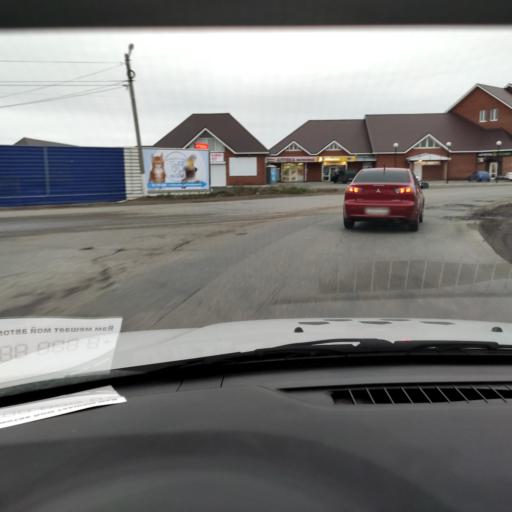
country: RU
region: Samara
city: Podstepki
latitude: 53.5160
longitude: 49.2166
